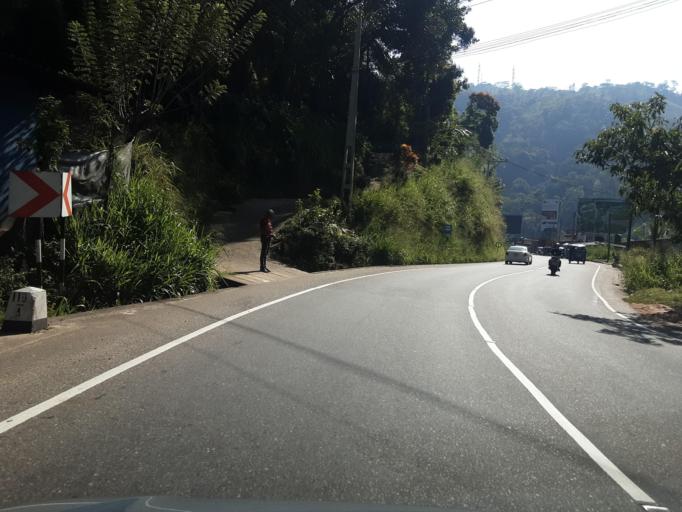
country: LK
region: Uva
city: Badulla
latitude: 6.9753
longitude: 81.0430
